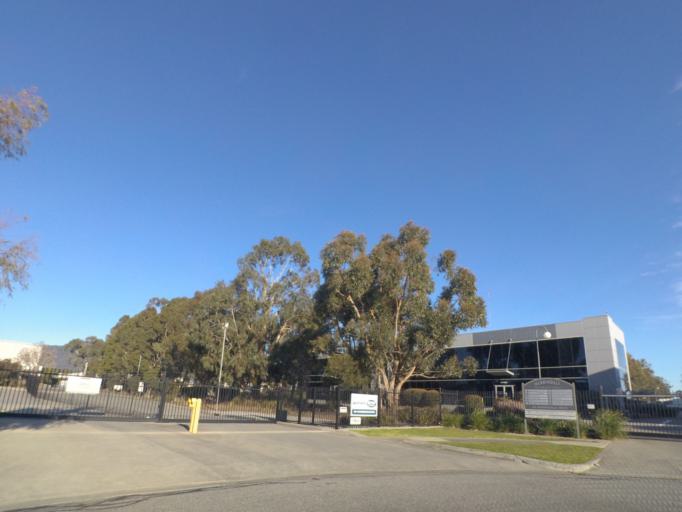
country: AU
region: Victoria
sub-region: Maroondah
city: Bayswater North
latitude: -37.8138
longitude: 145.2999
